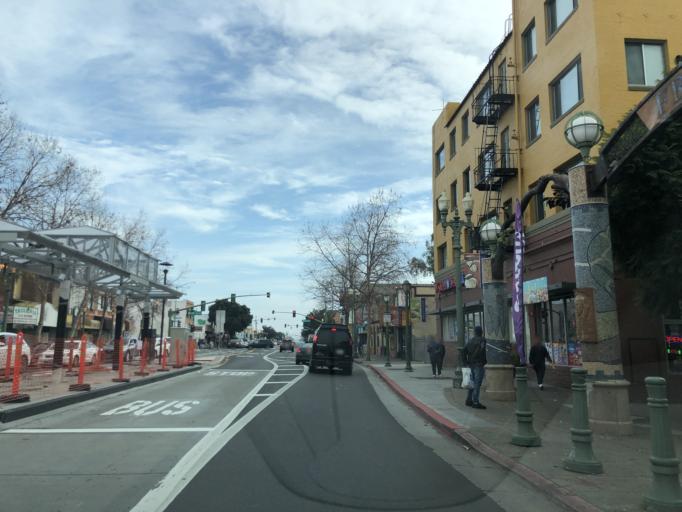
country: US
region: California
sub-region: Alameda County
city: Alameda
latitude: 37.7766
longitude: -122.2238
